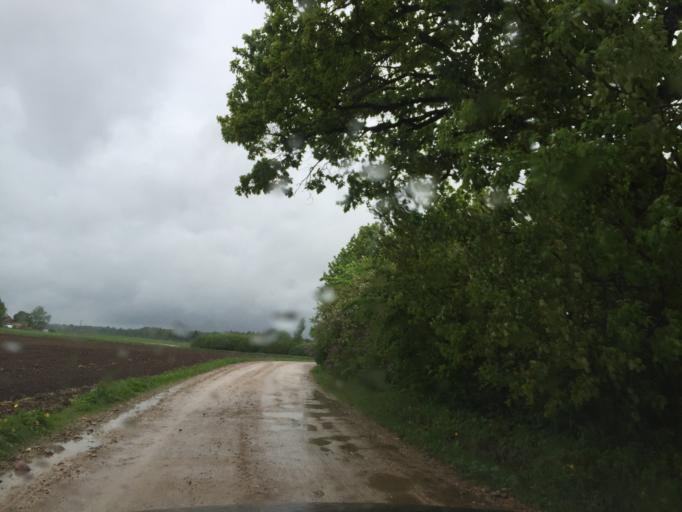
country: LV
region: Ogre
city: Jumprava
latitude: 56.6681
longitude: 24.9971
